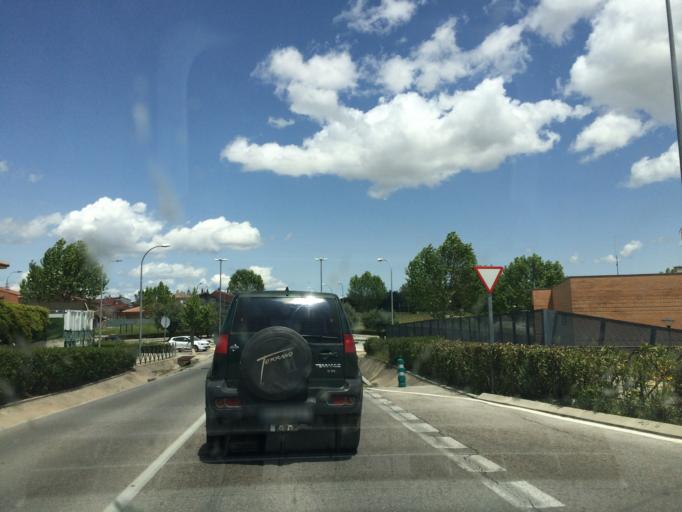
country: ES
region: Madrid
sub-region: Provincia de Madrid
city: Ribatejada
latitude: 40.6988
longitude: -3.4359
